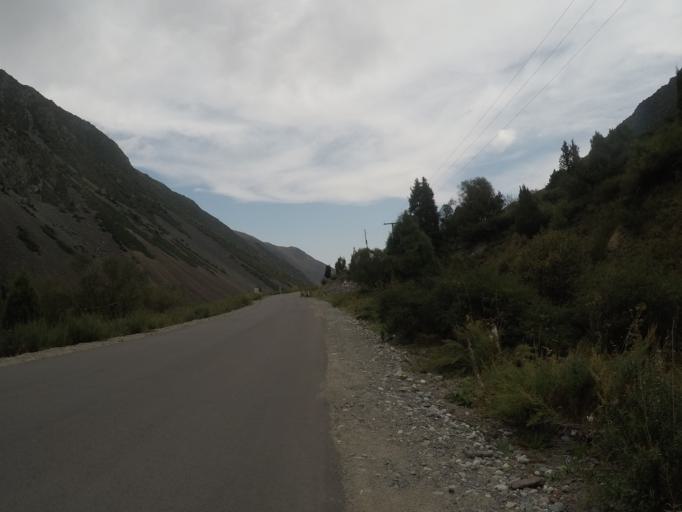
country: KG
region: Chuy
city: Bishkek
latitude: 42.5778
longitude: 74.4817
